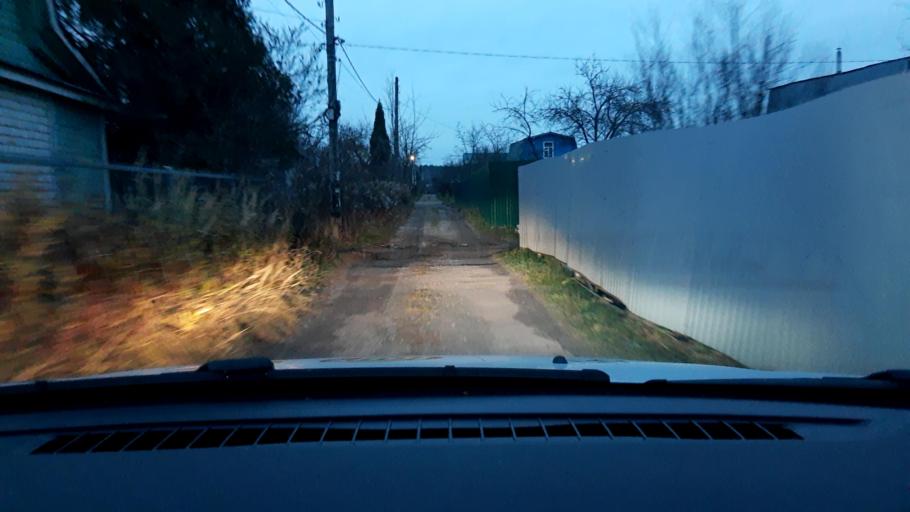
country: RU
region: Nizjnij Novgorod
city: Neklyudovo
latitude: 56.4282
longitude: 44.0097
